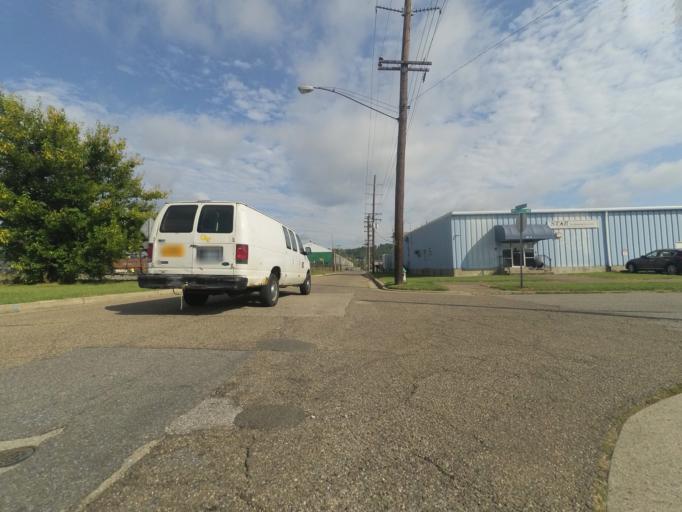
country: US
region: West Virginia
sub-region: Cabell County
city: Huntington
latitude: 38.4255
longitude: -82.4159
